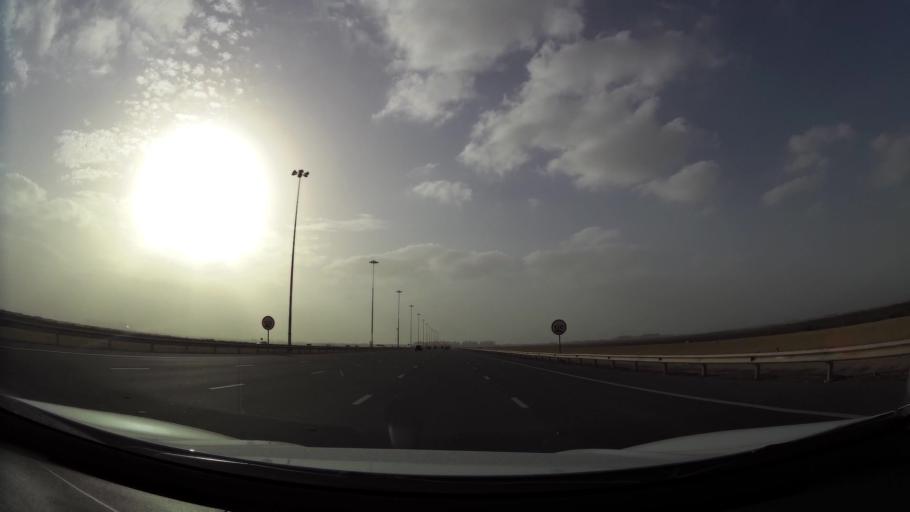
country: AE
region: Abu Dhabi
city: Abu Dhabi
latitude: 24.5471
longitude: 54.4725
